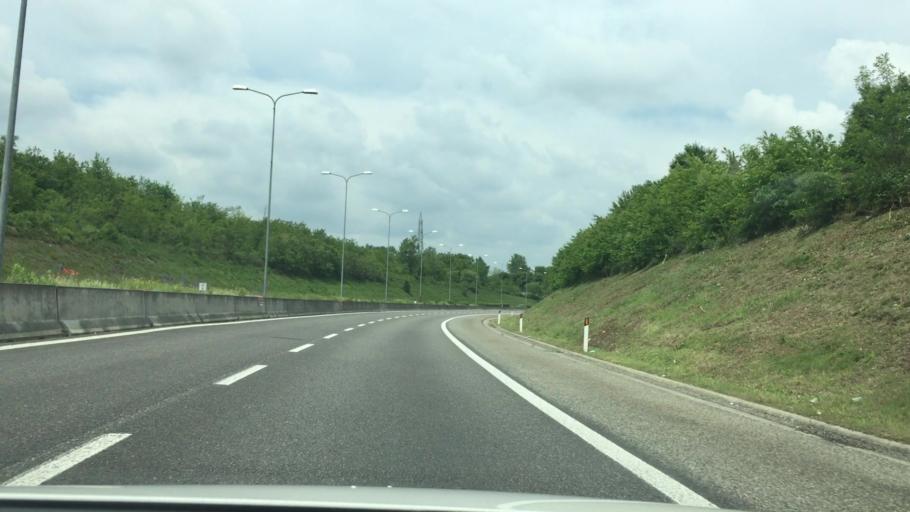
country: IT
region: Lombardy
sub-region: Provincia di Varese
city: Lonate Pozzolo
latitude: 45.5878
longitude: 8.7169
